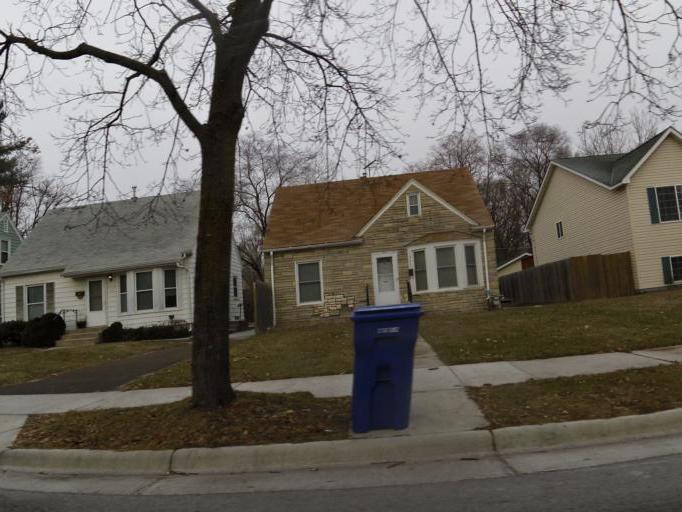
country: US
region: Minnesota
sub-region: Ramsey County
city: Maplewood
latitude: 44.9568
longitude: -93.0426
